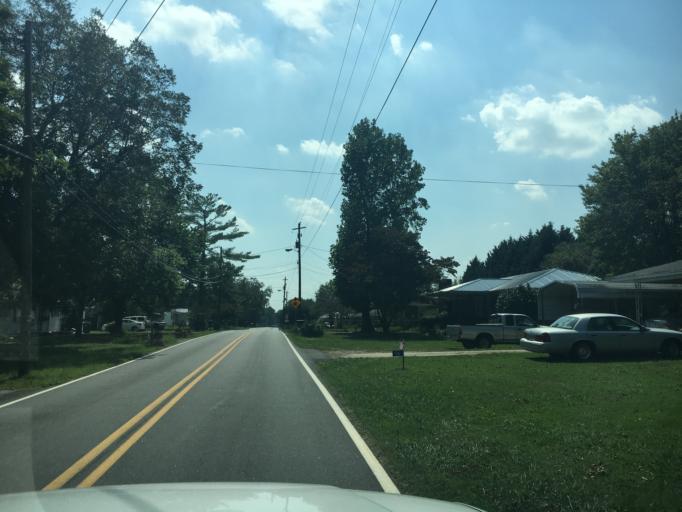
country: US
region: Georgia
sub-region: Hart County
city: Hartwell
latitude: 34.3527
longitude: -82.9191
